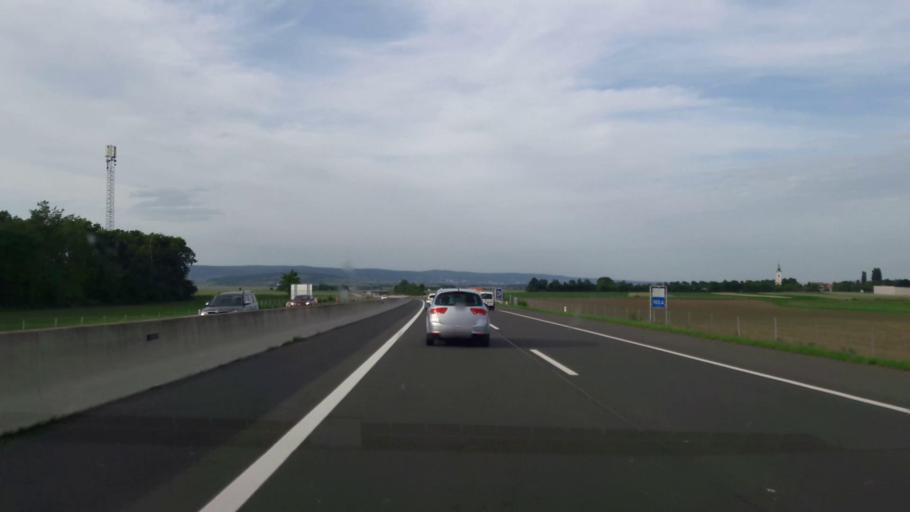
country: AT
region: Burgenland
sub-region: Politischer Bezirk Mattersburg
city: Krensdorf
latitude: 47.7684
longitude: 16.4243
